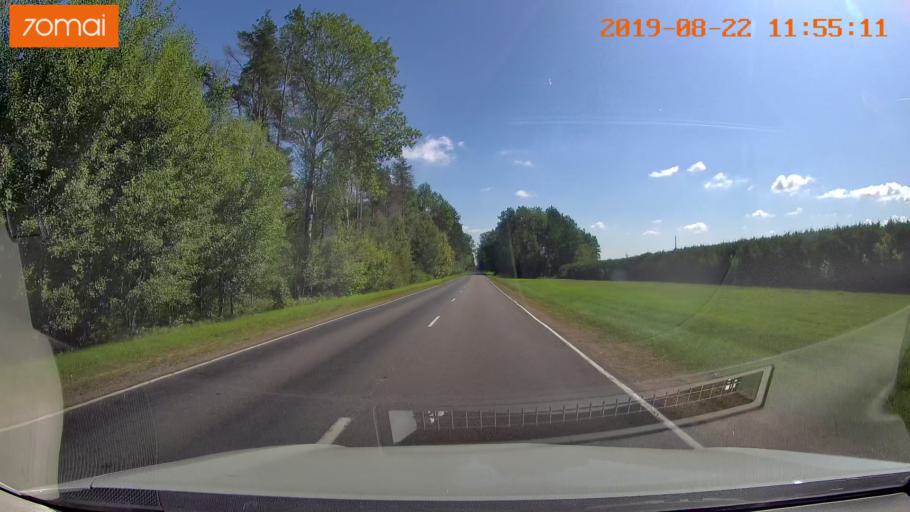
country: BY
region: Minsk
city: Prawdzinski
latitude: 53.4324
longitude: 27.5418
